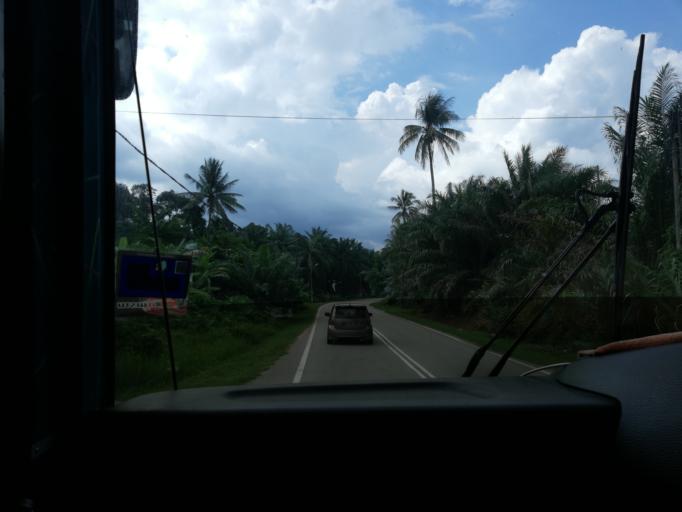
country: MY
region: Kedah
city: Kulim
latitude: 5.2379
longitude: 100.6017
